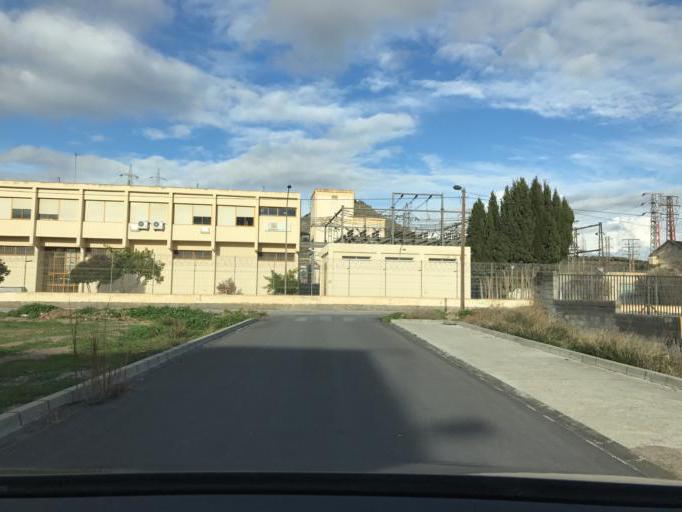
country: ES
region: Andalusia
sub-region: Provincia de Granada
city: Atarfe
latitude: 37.2239
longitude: -3.6977
